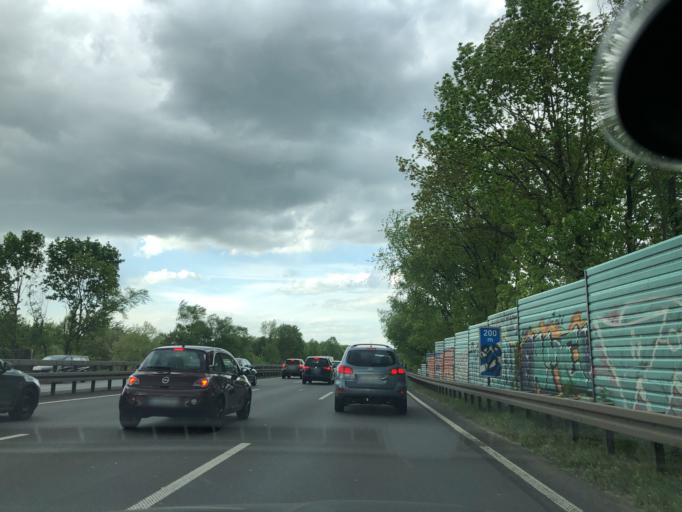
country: DE
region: North Rhine-Westphalia
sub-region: Regierungsbezirk Koln
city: Bonn
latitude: 50.7448
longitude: 7.1430
